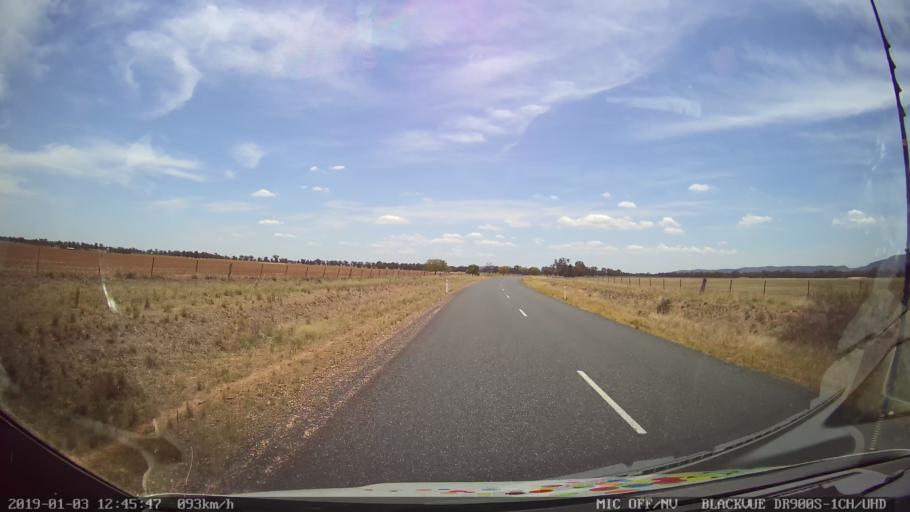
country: AU
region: New South Wales
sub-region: Weddin
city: Grenfell
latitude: -33.7451
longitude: 148.2262
